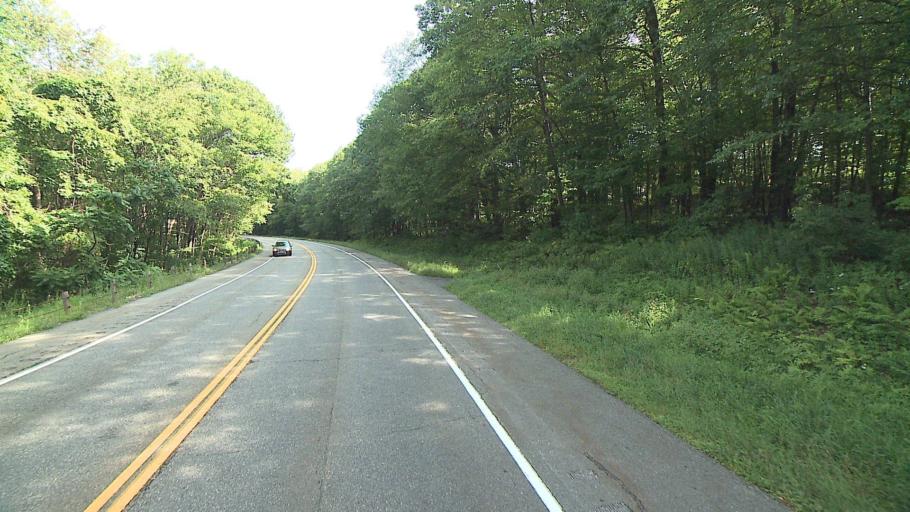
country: US
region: Connecticut
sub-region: Litchfield County
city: Litchfield
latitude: 41.7525
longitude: -73.1578
